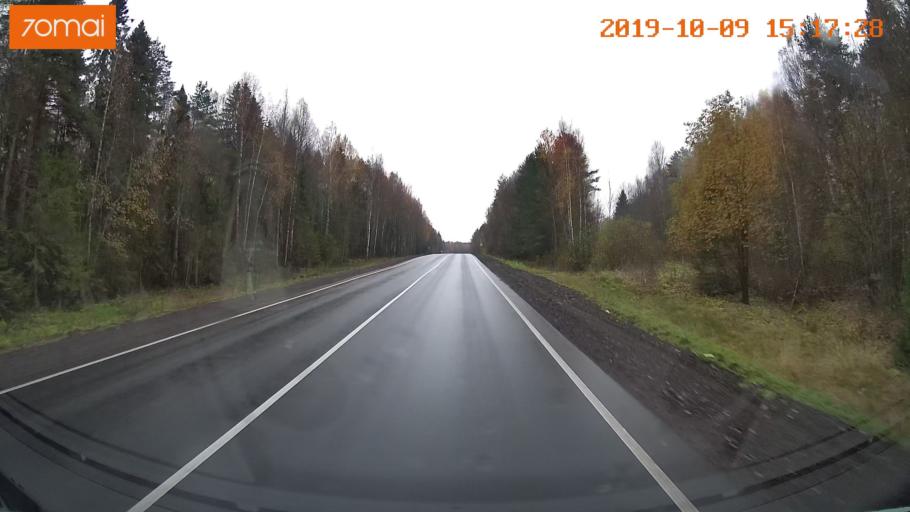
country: RU
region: Kostroma
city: Susanino
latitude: 58.0980
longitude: 41.5826
